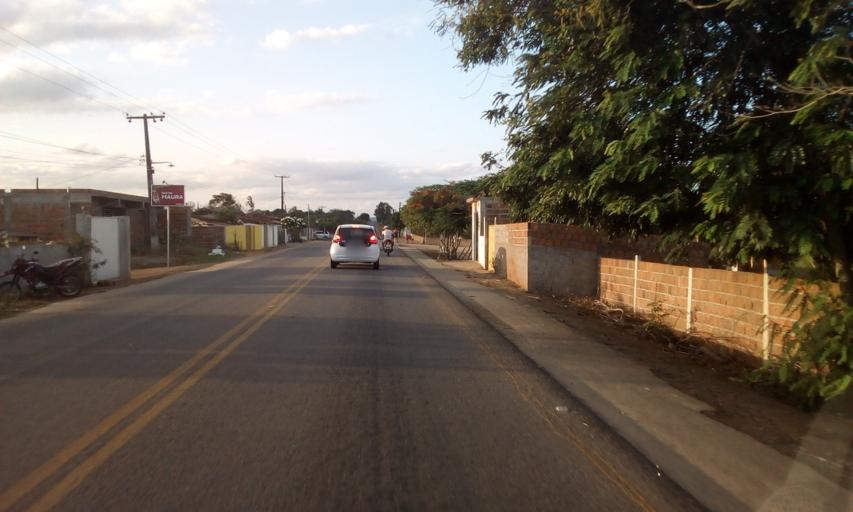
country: BR
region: Paraiba
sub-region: Guarabira
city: Guarabira
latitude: -6.9040
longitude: -35.4575
